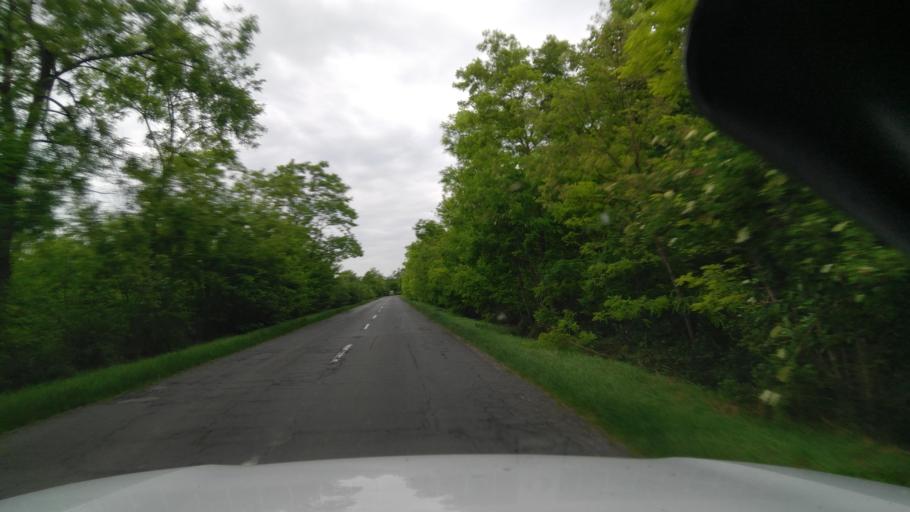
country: HU
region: Bekes
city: Bekescsaba
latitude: 46.6791
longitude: 21.1682
